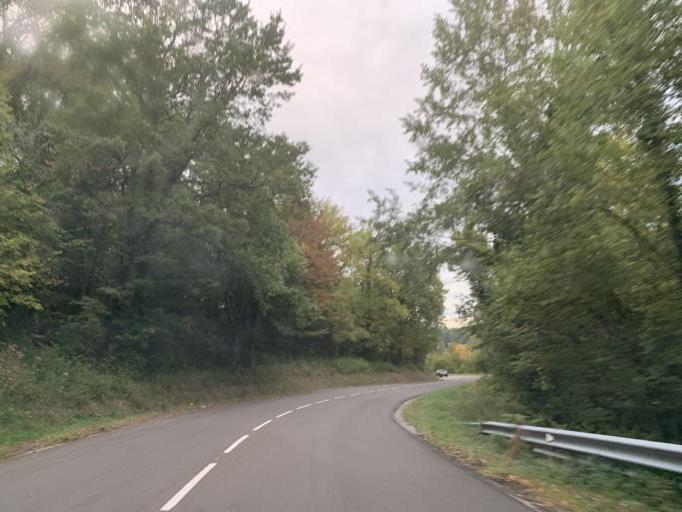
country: FR
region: Rhone-Alpes
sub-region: Departement de l'Ain
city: Belley
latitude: 45.7041
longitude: 5.6554
